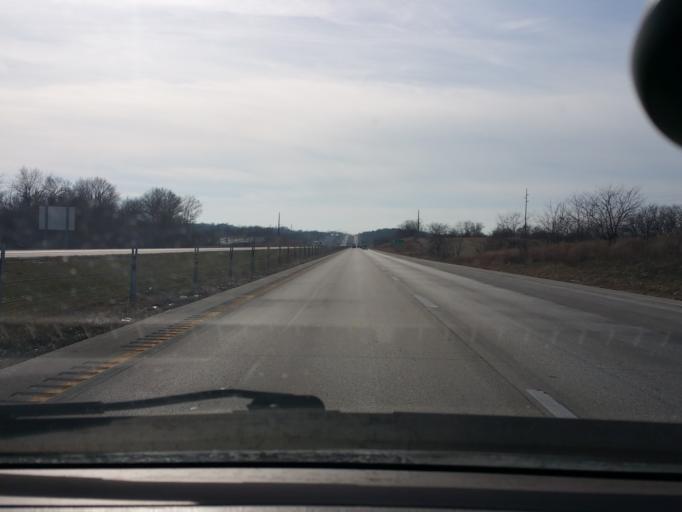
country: US
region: Missouri
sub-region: Clay County
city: Kearney
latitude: 39.3594
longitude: -94.3770
